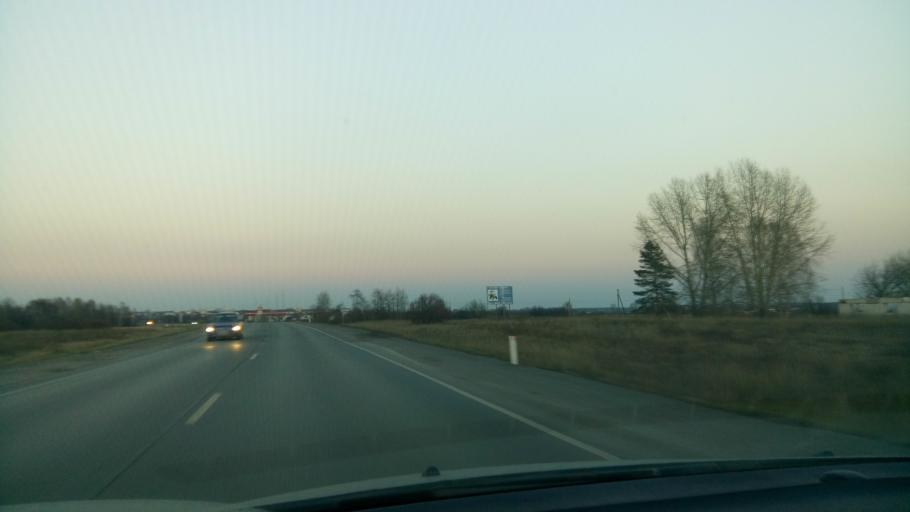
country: RU
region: Sverdlovsk
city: Pyshma
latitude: 56.9385
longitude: 63.2113
